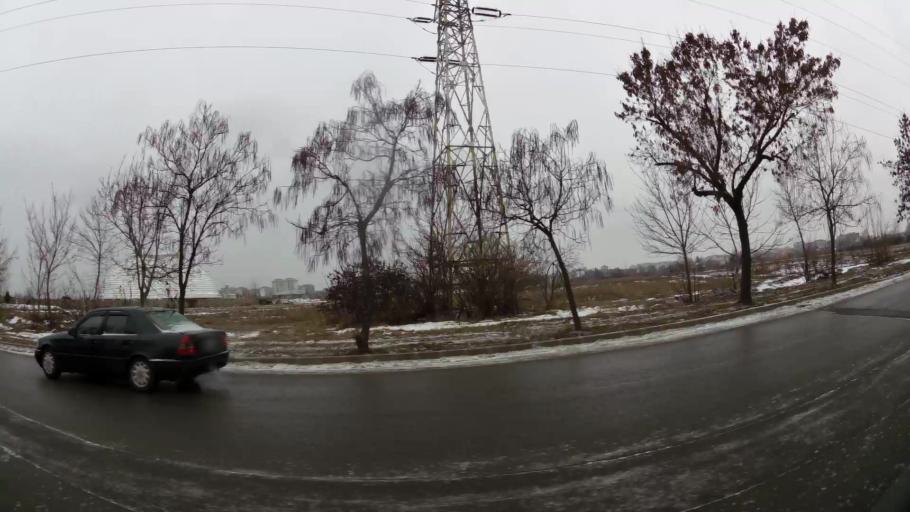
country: RO
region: Dambovita
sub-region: Municipiul Targoviste
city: Targoviste
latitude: 44.9292
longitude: 25.4792
